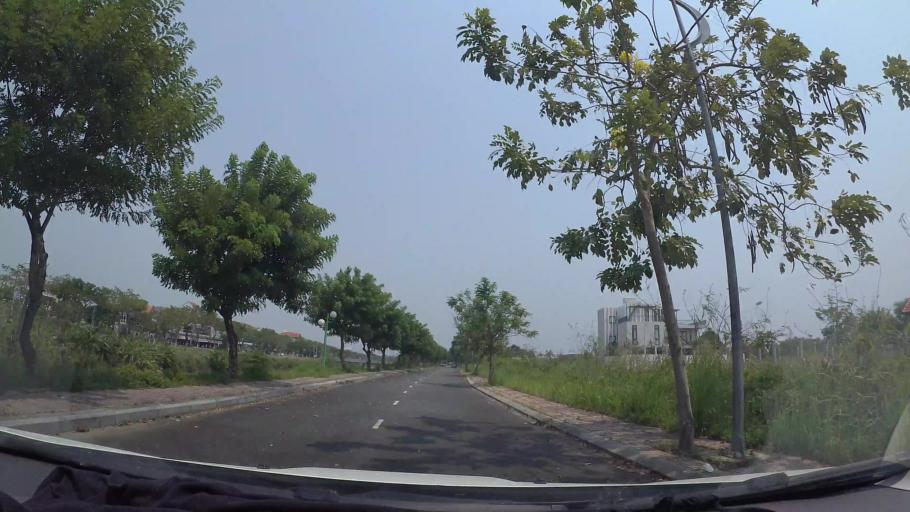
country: VN
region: Da Nang
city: Cam Le
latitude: 16.0132
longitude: 108.2091
